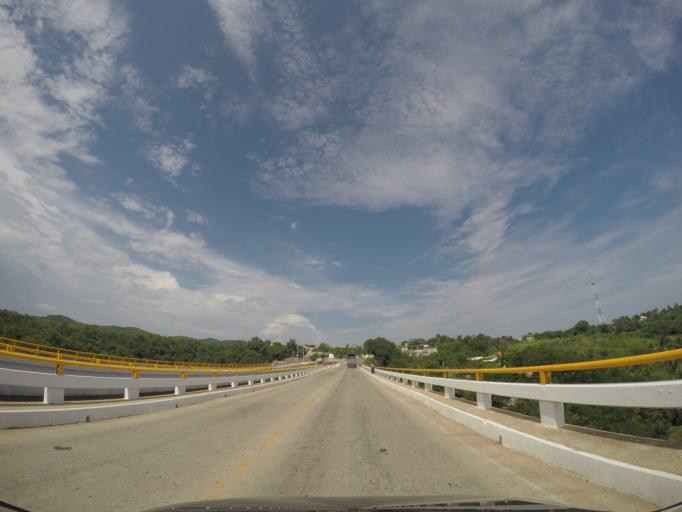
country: MX
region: Oaxaca
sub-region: Santa Maria Colotepec
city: Brisas de Zicatela
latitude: 15.8273
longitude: -97.0260
